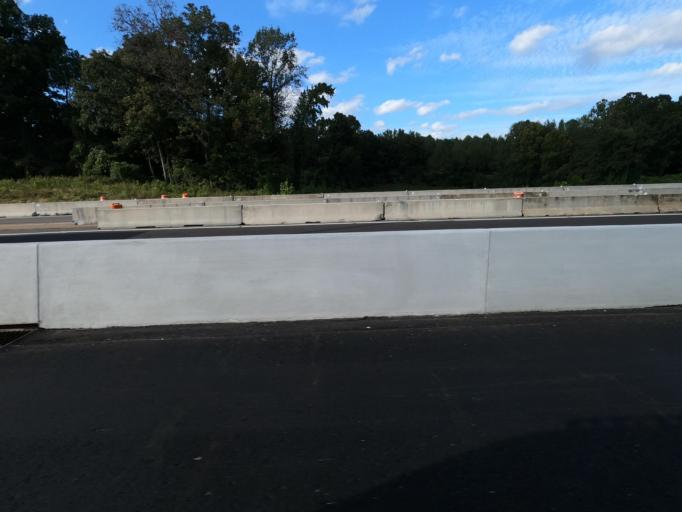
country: US
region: Tennessee
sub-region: Madison County
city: Jackson
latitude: 35.6730
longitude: -88.8121
